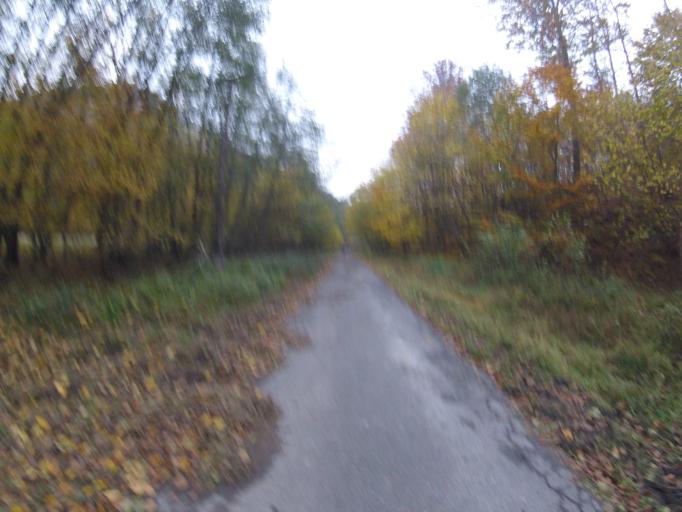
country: HU
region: Borsod-Abauj-Zemplen
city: Tolcsva
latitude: 48.4235
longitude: 21.4261
